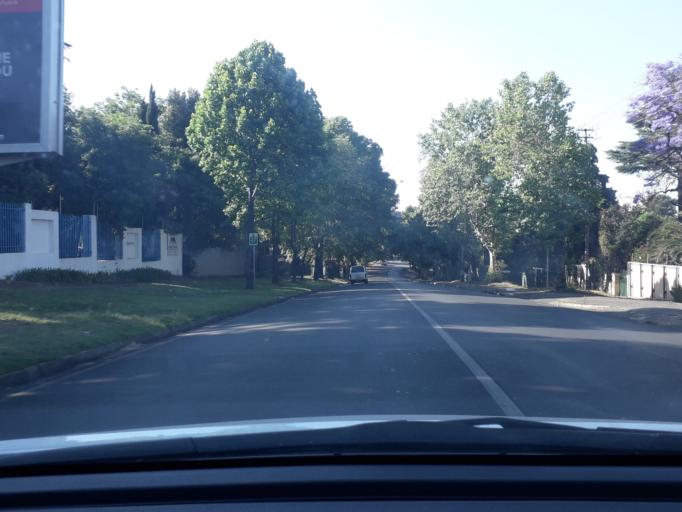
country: ZA
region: Gauteng
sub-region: City of Johannesburg Metropolitan Municipality
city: Johannesburg
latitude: -26.1394
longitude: 28.0349
